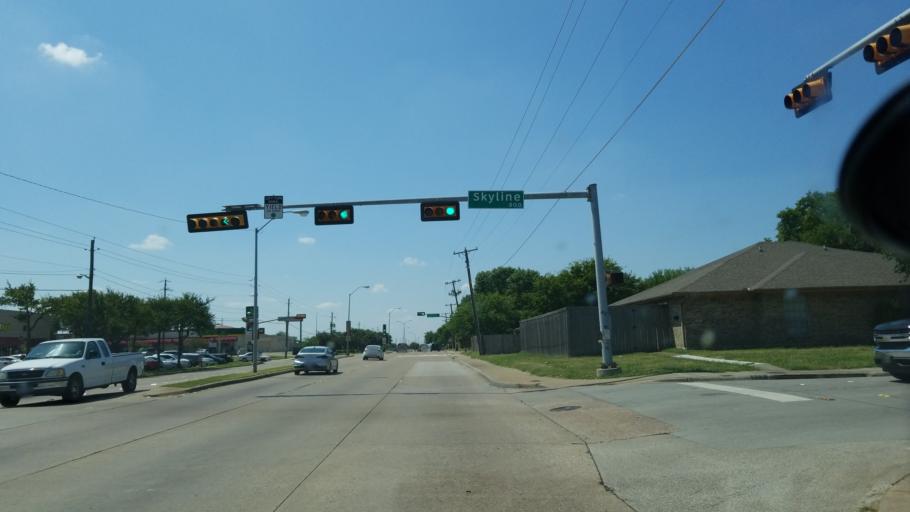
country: US
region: Texas
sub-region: Dallas County
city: Duncanville
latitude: 32.6577
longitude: -96.8915
